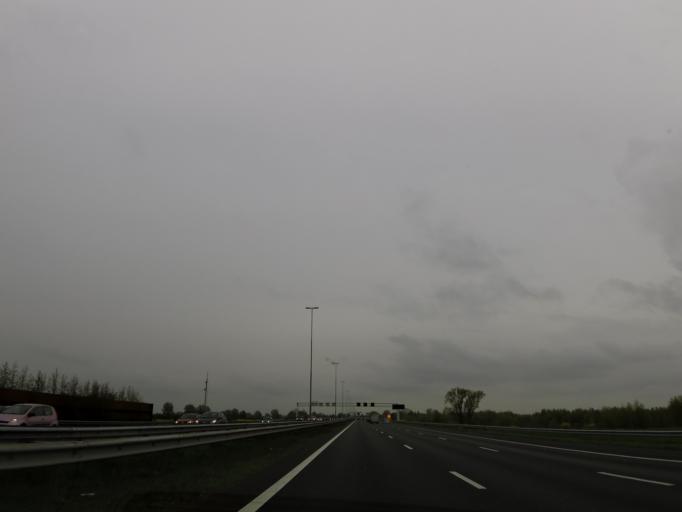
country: NL
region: Gelderland
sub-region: Gemeente Maasdriel
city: Hedel
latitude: 51.7485
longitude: 5.2939
